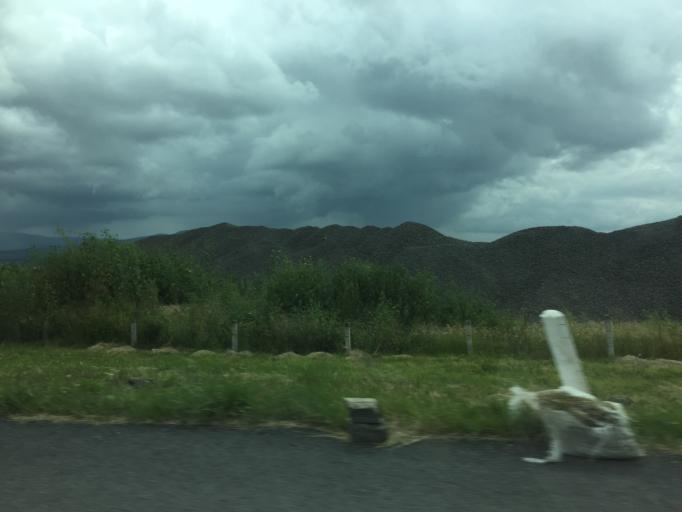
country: MX
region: Jalisco
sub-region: Zapotlanejo
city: La Mezquitera
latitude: 20.5907
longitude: -103.1047
